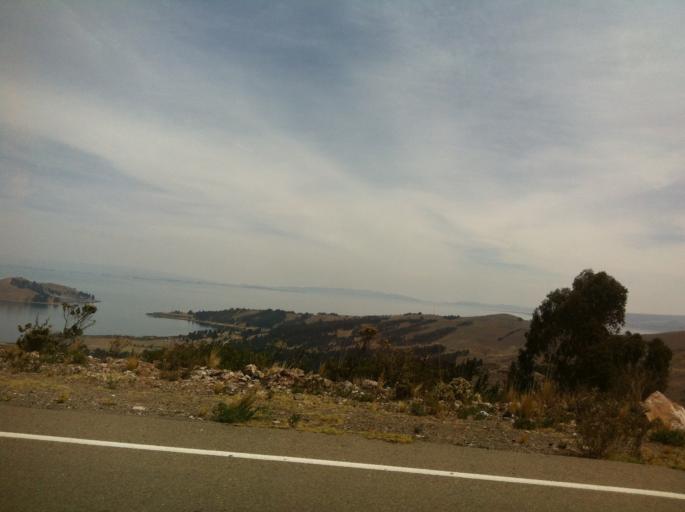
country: BO
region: La Paz
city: San Pedro
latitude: -16.1888
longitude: -68.9699
